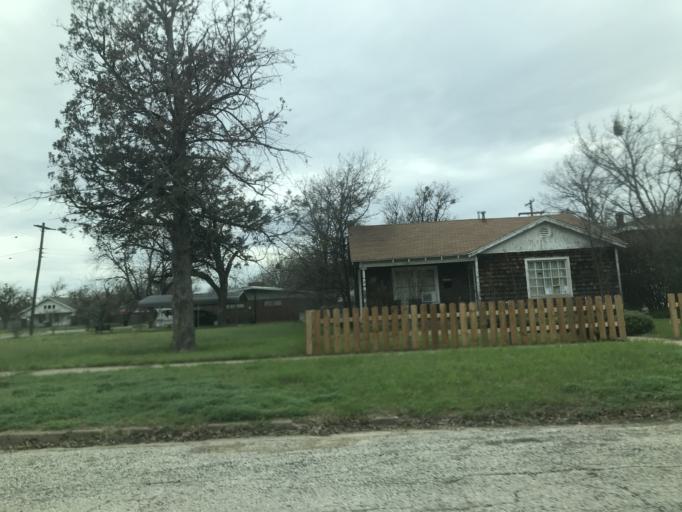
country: US
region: Texas
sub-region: Taylor County
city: Abilene
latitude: 32.4562
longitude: -99.7455
